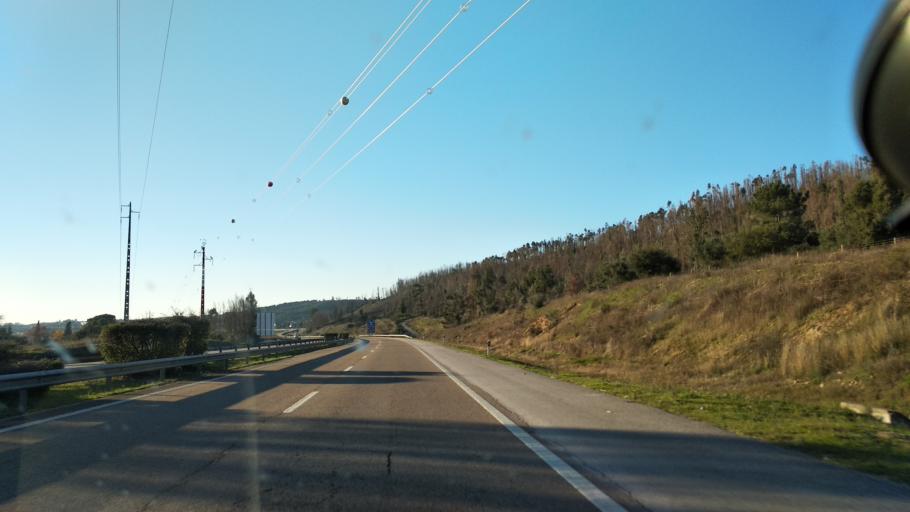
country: PT
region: Santarem
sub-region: Abrantes
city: Tramagal
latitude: 39.4840
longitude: -8.2484
